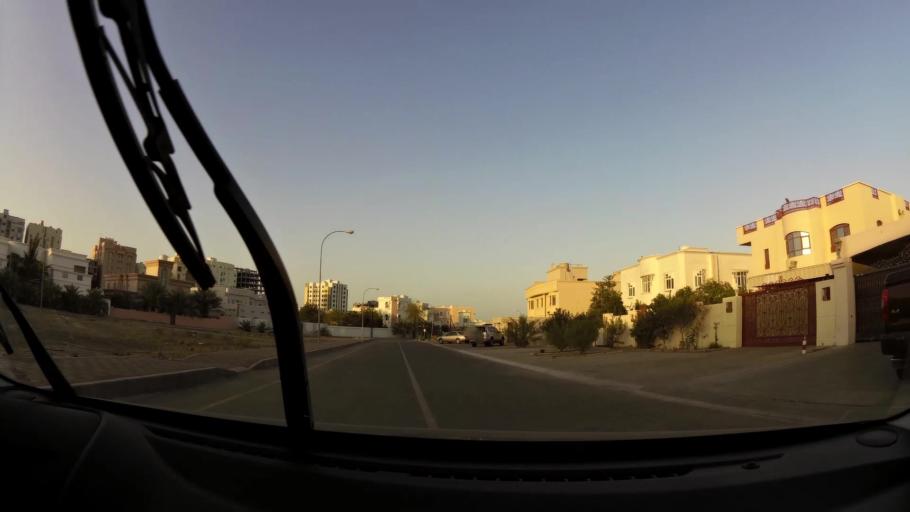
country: OM
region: Muhafazat Masqat
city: As Sib al Jadidah
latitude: 23.6129
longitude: 58.2033
